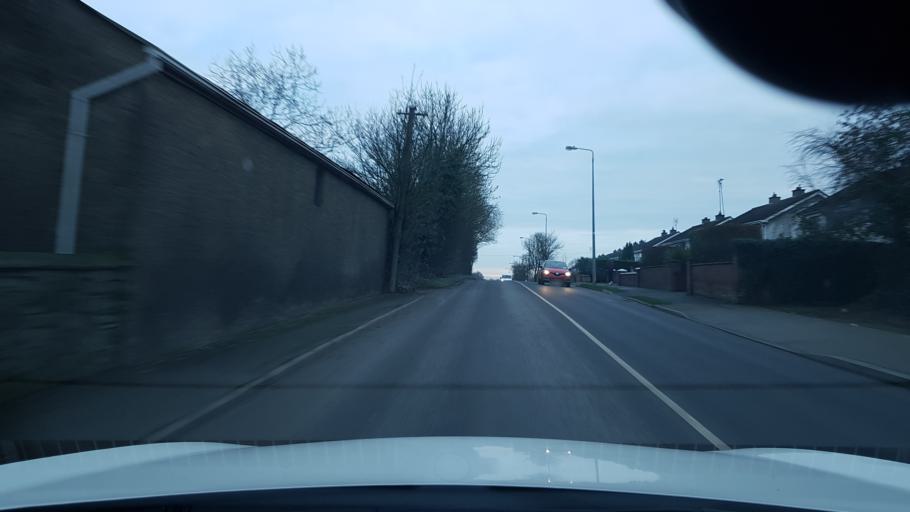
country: IE
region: Leinster
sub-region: An Mhi
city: Navan
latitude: 53.6669
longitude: -6.6802
